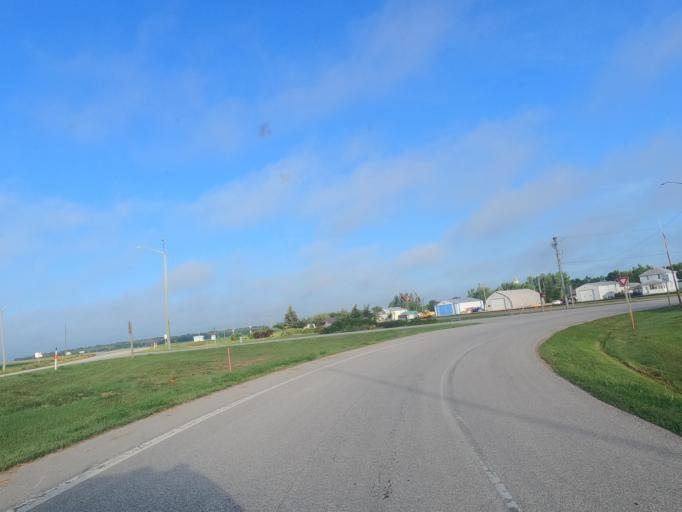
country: CA
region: Manitoba
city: Headingley
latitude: 49.7689
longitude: -97.6179
